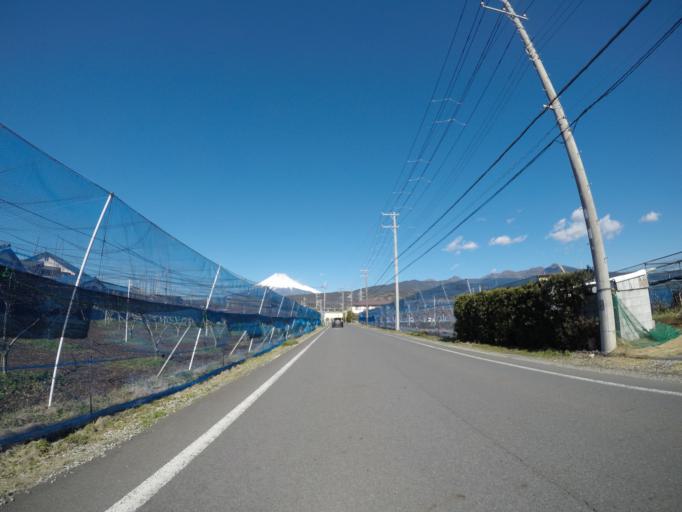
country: JP
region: Shizuoka
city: Fuji
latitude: 35.1508
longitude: 138.7412
